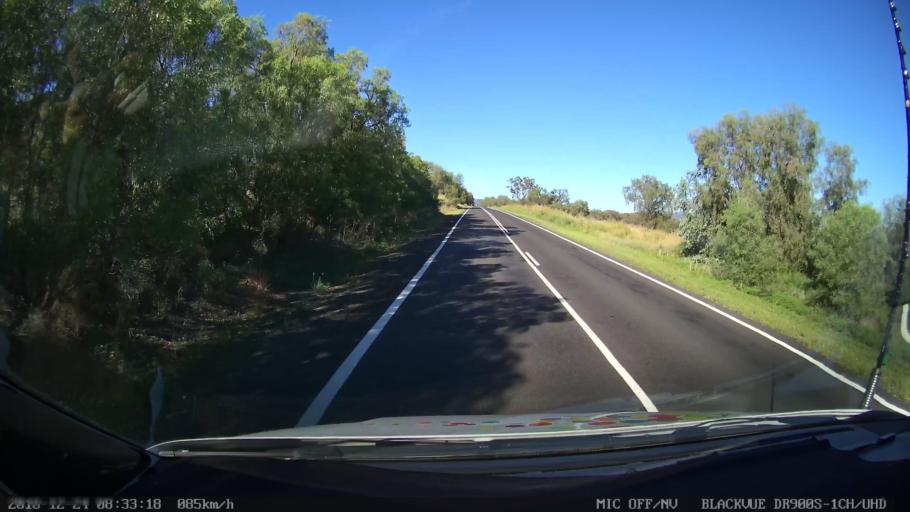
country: AU
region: New South Wales
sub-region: Liverpool Plains
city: Quirindi
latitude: -31.2854
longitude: 150.6863
